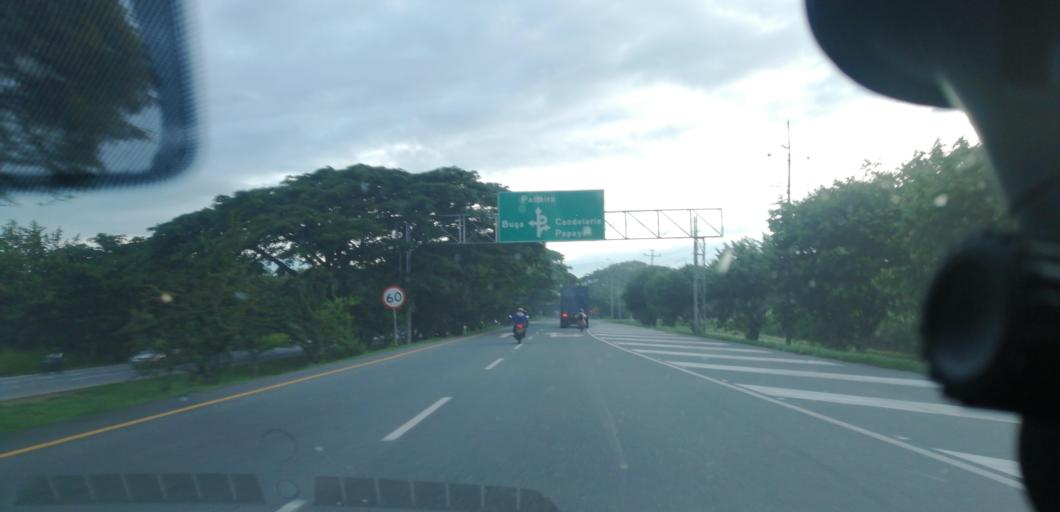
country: CO
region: Valle del Cauca
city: Palmira
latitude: 3.5236
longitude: -76.3413
